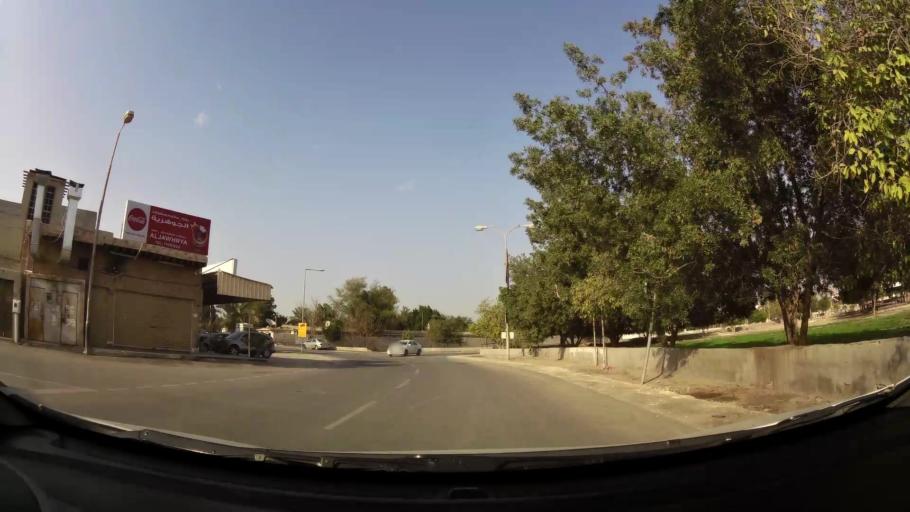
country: BH
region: Manama
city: Jidd Hafs
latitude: 26.2181
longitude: 50.5040
